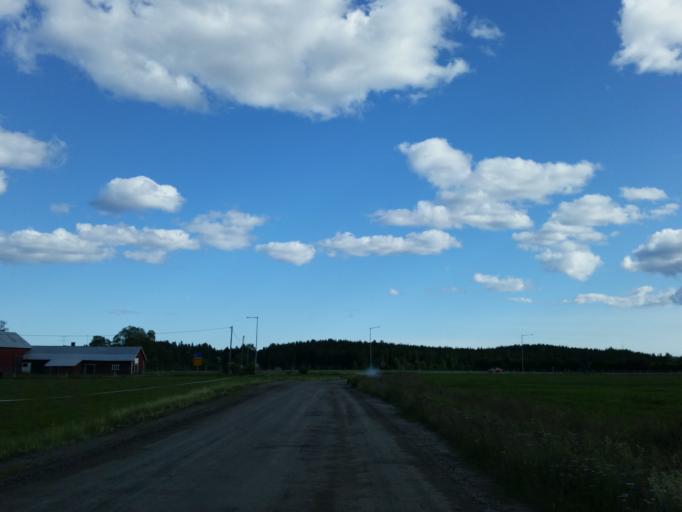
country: SE
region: Vaesterbotten
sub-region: Robertsfors Kommun
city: Robertsfors
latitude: 64.1296
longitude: 20.8861
